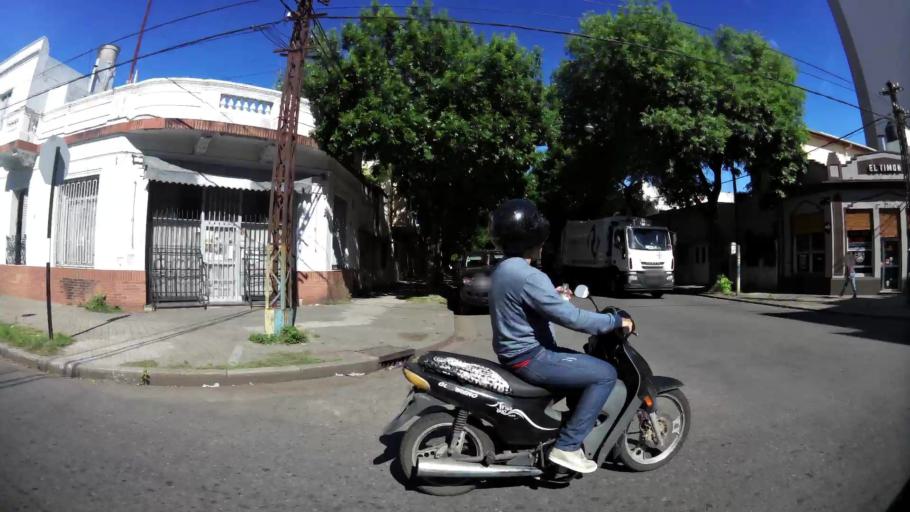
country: AR
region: Santa Fe
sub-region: Departamento de Rosario
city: Rosario
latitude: -32.9429
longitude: -60.6730
